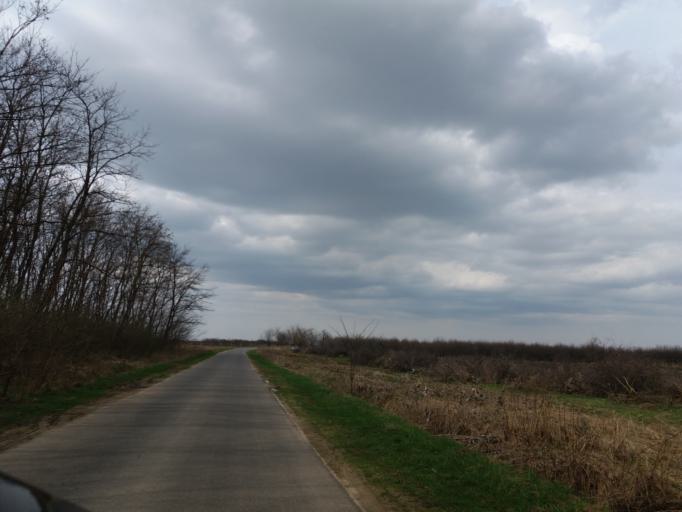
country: HU
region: Szabolcs-Szatmar-Bereg
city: Nyirtass
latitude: 48.0909
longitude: 22.0327
